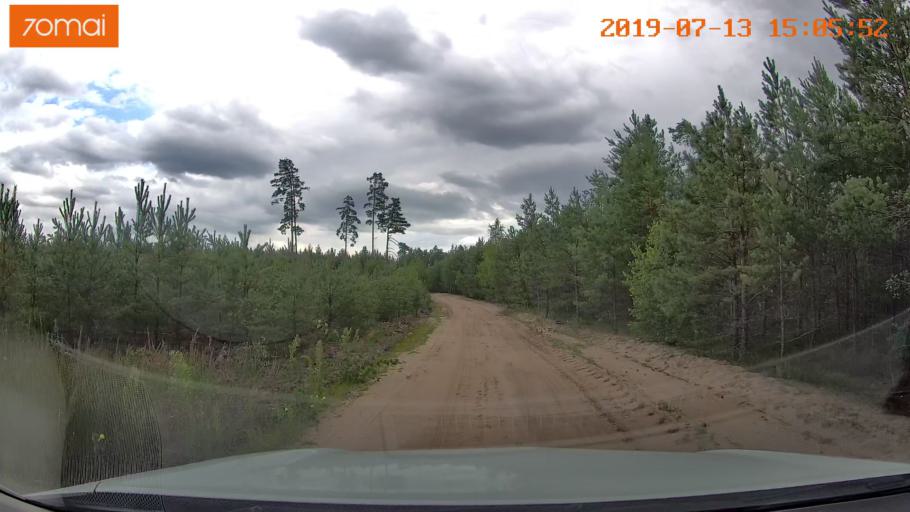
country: BY
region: Mogilev
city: Asipovichy
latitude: 53.2013
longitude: 28.7533
